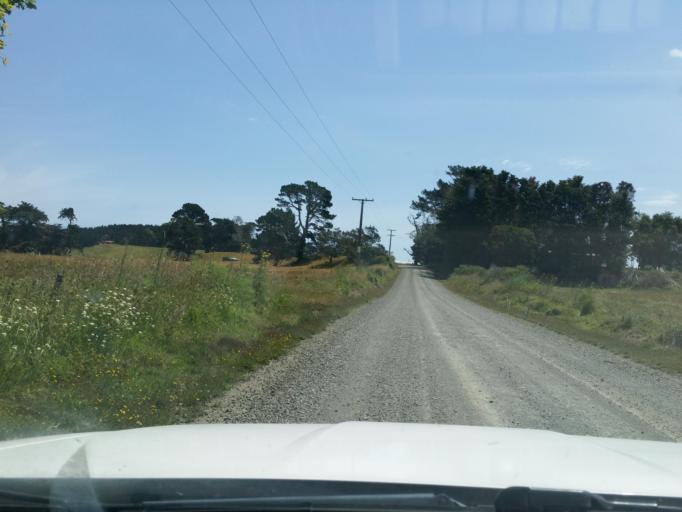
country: NZ
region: Northland
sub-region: Kaipara District
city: Dargaville
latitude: -35.9064
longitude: 173.8051
